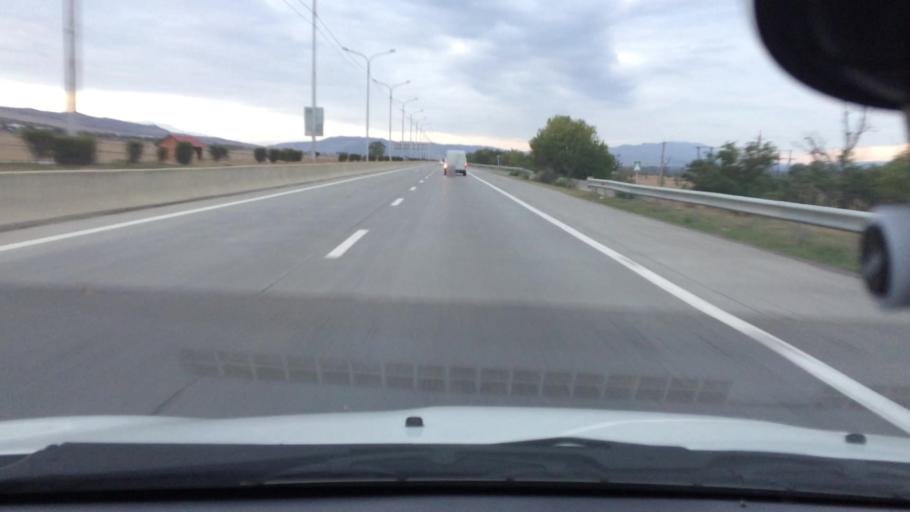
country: GE
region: Mtskheta-Mtianeti
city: Mtskheta
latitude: 41.8942
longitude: 44.6620
